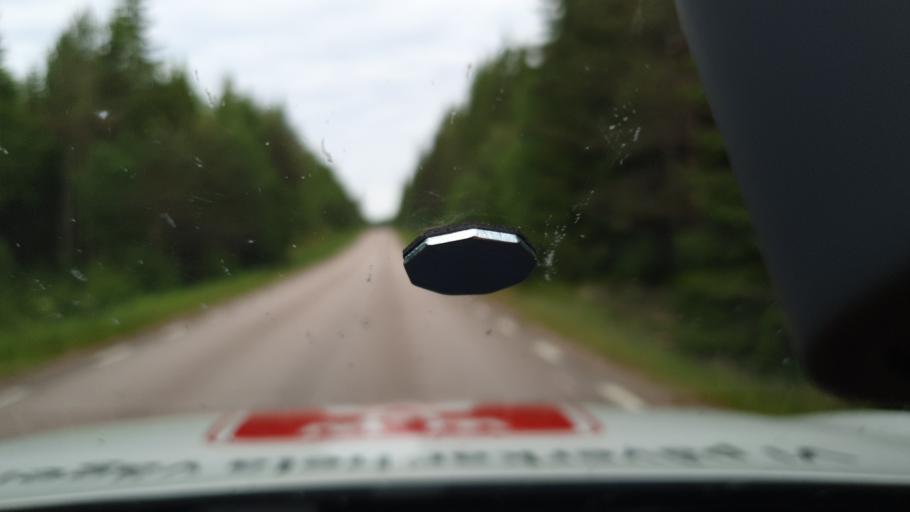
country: SE
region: Vaermland
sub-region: Torsby Kommun
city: Torsby
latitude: 60.1138
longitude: 12.9274
